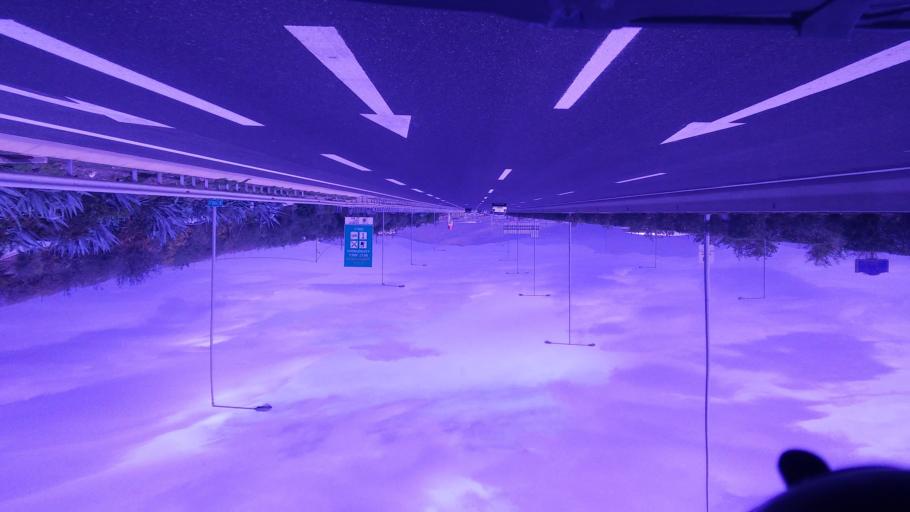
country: GR
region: Attica
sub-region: Nomarchia Dytikis Attikis
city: Aspropyrgos
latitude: 38.0910
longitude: 23.6157
